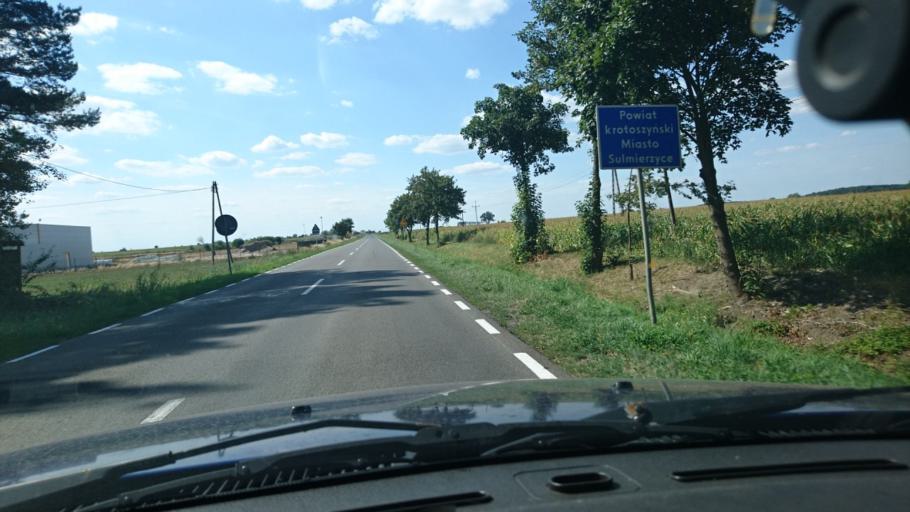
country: PL
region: Greater Poland Voivodeship
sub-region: Powiat krotoszynski
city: Sulmierzyce
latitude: 51.6036
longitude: 17.5728
